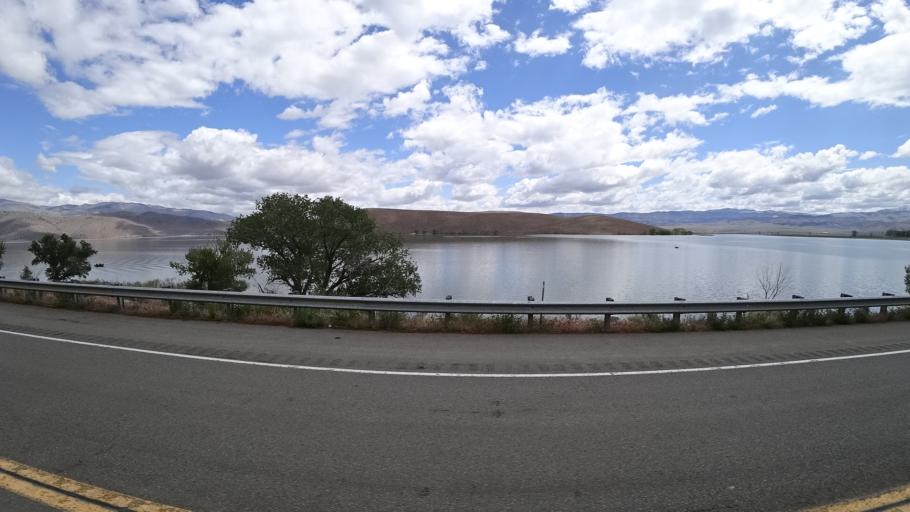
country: US
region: Nevada
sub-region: Lyon County
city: Smith Valley
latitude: 38.6648
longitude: -119.5428
